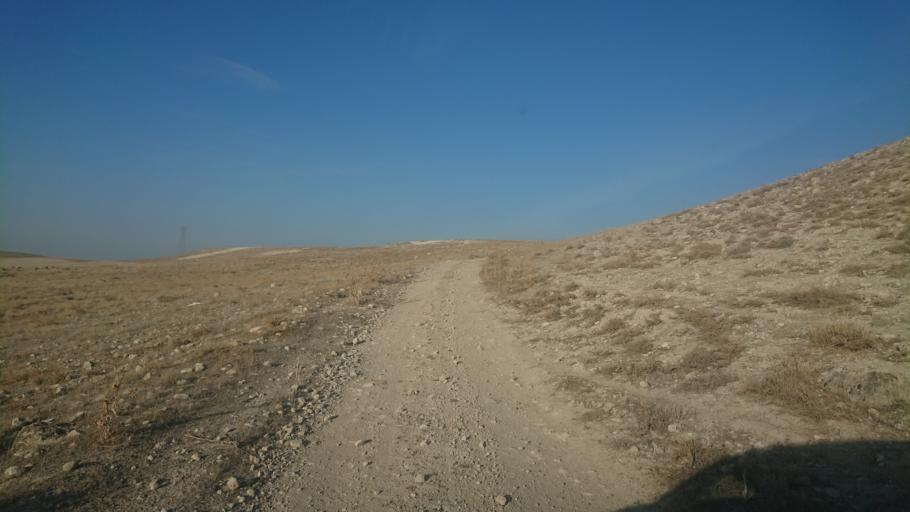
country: TR
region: Aksaray
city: Sultanhani
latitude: 38.1443
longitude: 33.5847
